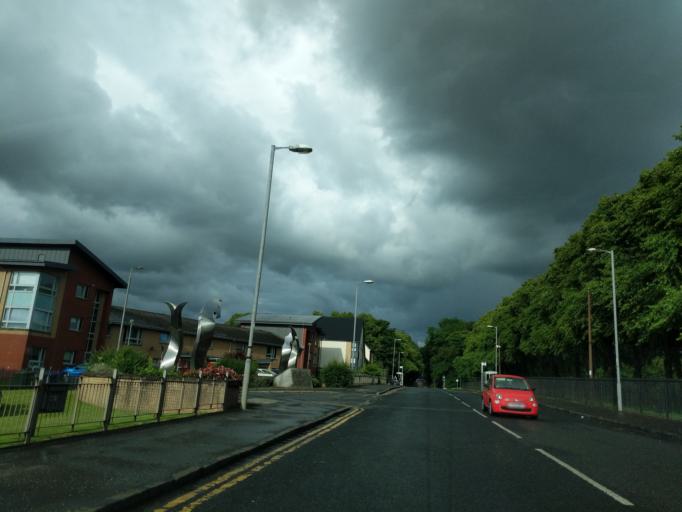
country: GB
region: Scotland
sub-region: East Renfrewshire
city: Barrhead
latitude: 55.8045
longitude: -4.3793
